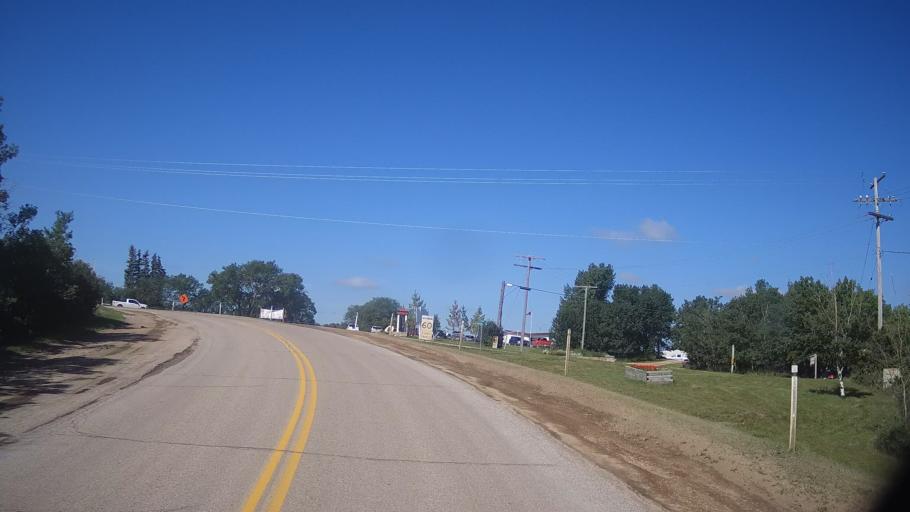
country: CA
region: Saskatchewan
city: Watrous
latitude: 51.7191
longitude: -105.4505
